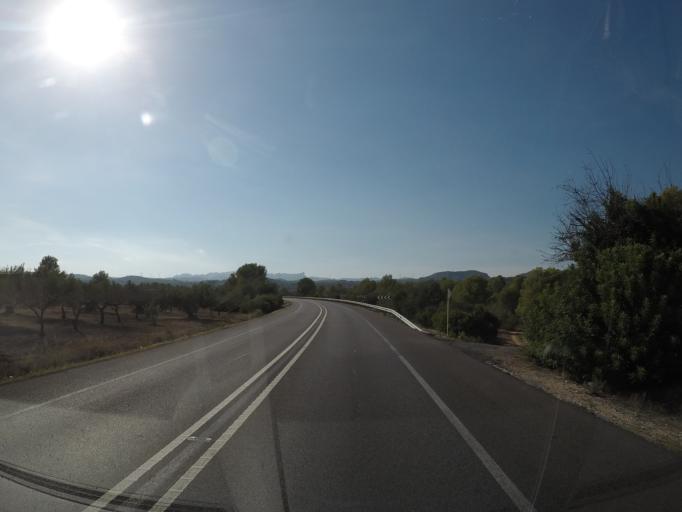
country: ES
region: Catalonia
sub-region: Provincia de Tarragona
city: El Perello
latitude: 40.8977
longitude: 0.7362
